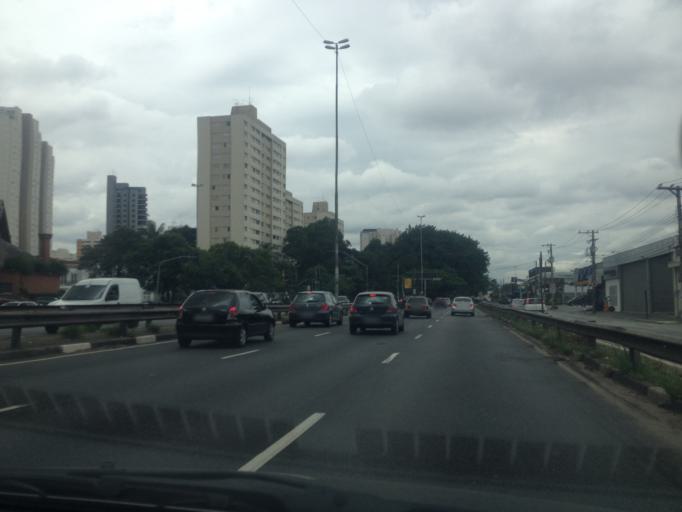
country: BR
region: Sao Paulo
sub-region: Sao Paulo
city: Sao Paulo
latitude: -23.6007
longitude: -46.6838
